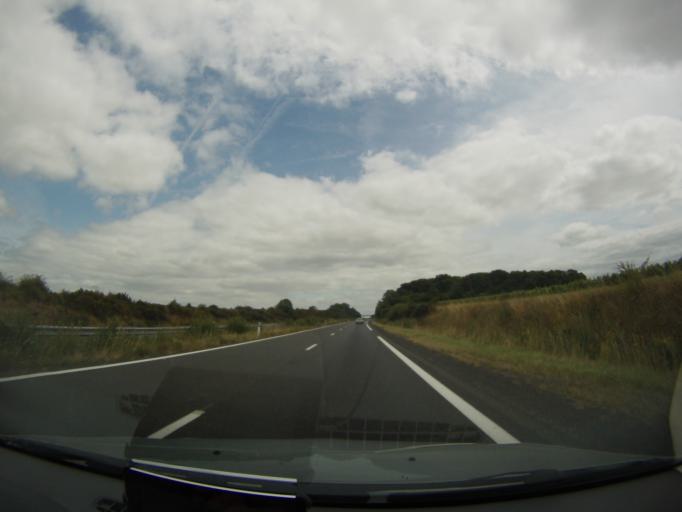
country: FR
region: Pays de la Loire
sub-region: Departement de la Loire-Atlantique
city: Vallet
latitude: 47.1555
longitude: -1.2474
